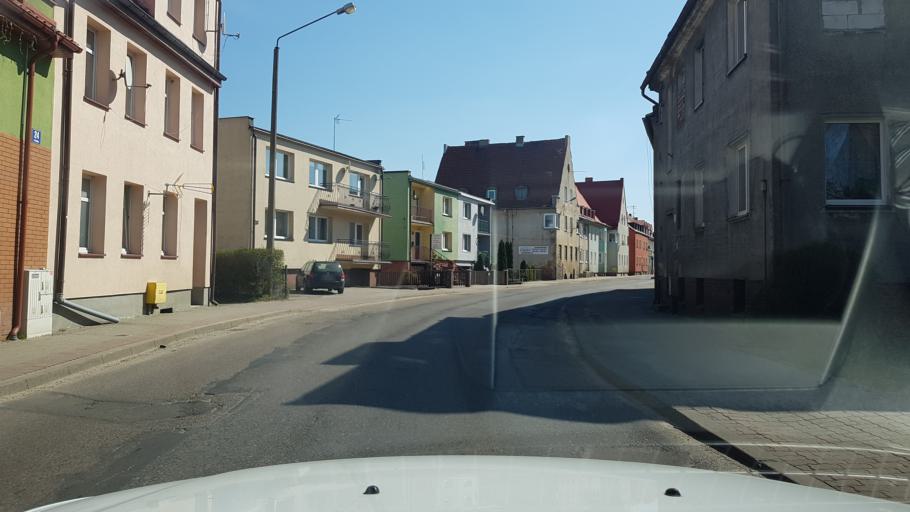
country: PL
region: West Pomeranian Voivodeship
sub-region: Powiat slawienski
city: Slawno
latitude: 54.3666
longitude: 16.6760
